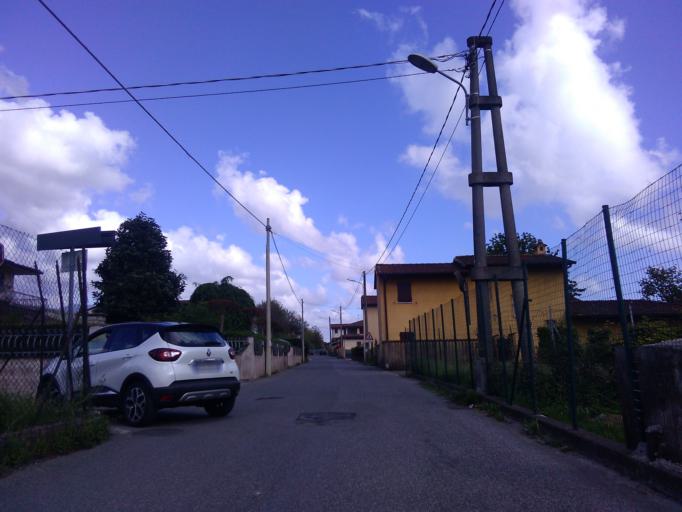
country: IT
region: Tuscany
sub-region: Provincia di Massa-Carrara
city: Capanne-Prato-Cinquale
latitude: 44.0056
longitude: 10.1498
